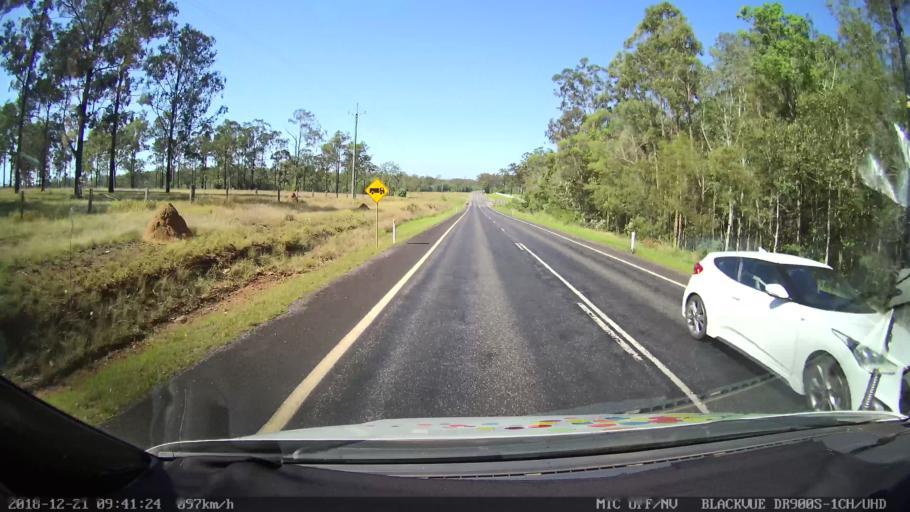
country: AU
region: New South Wales
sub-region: Clarence Valley
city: Grafton
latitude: -29.5846
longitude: 152.9576
